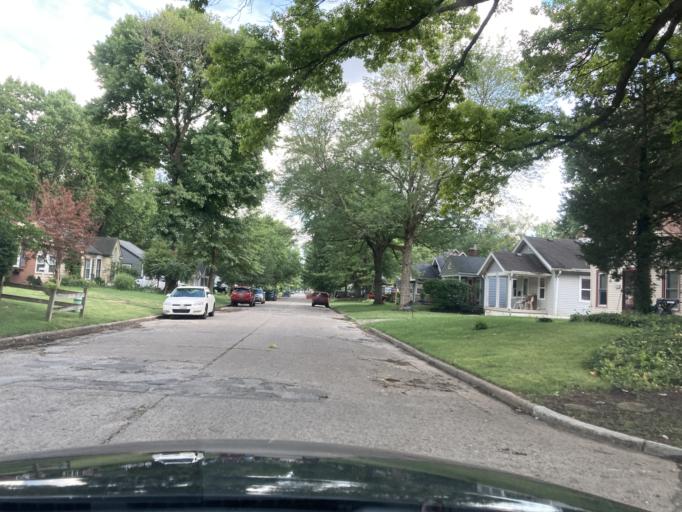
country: US
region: Indiana
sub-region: Marion County
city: Broad Ripple
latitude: 39.8453
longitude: -86.1291
